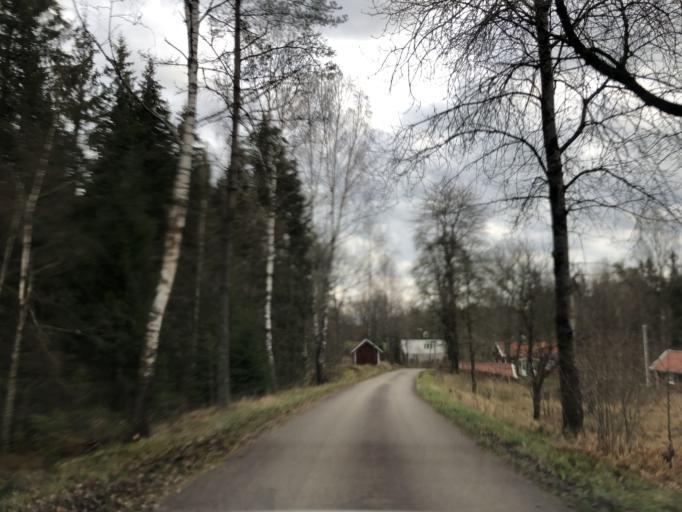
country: SE
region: Vaestra Goetaland
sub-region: Ulricehamns Kommun
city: Ulricehamn
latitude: 57.7273
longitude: 13.3276
